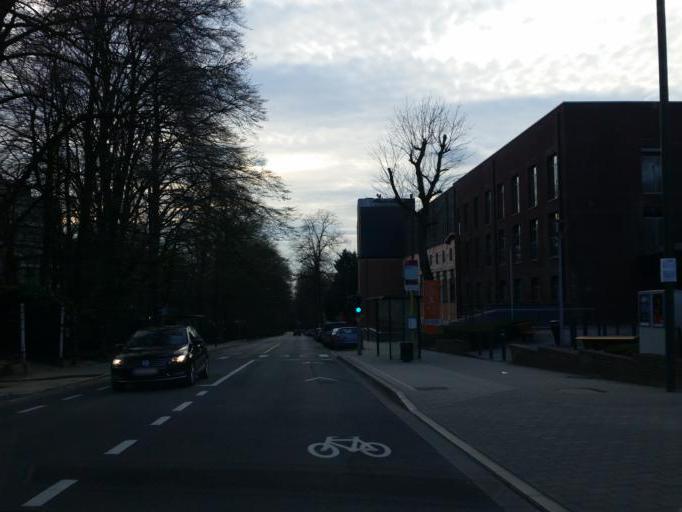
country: BE
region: Flanders
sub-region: Provincie Vlaams-Brabant
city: Linkebeek
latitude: 50.8050
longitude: 4.3694
